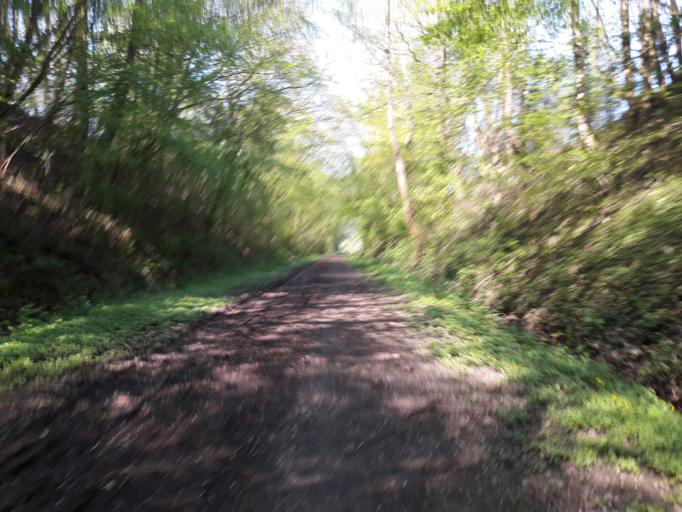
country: FR
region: Nord-Pas-de-Calais
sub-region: Departement du Nord
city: Sains-du-Nord
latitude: 50.1606
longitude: 4.0711
